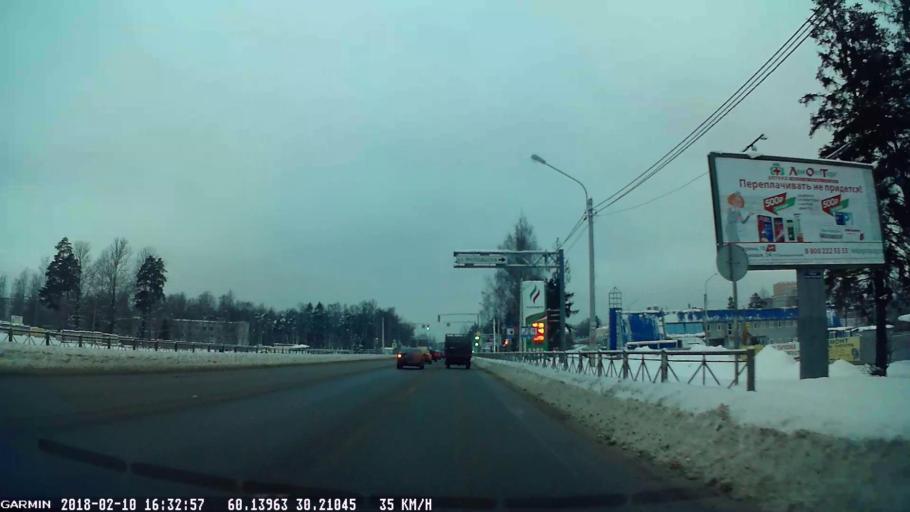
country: RU
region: Leningrad
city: Sertolovo
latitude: 60.1402
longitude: 30.2098
